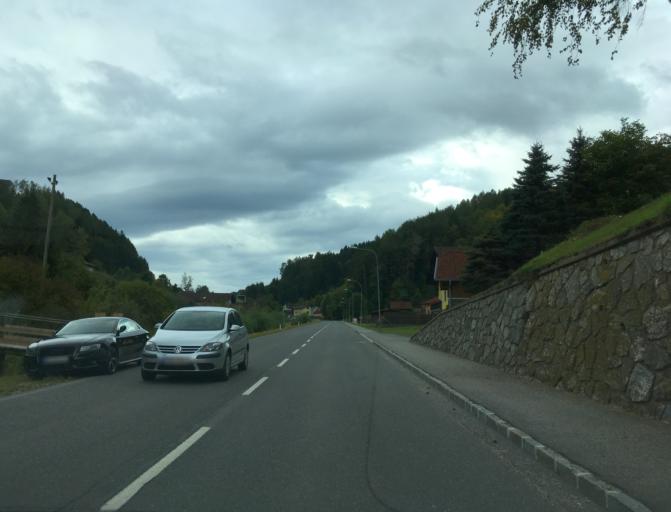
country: AT
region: Lower Austria
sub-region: Politischer Bezirk Neunkirchen
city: Thomasberg
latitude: 47.5723
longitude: 16.1427
